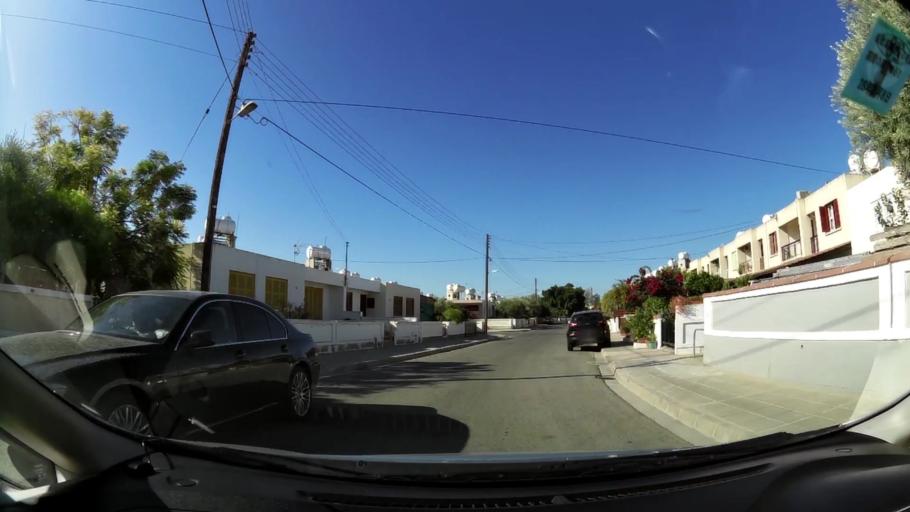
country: CY
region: Larnaka
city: Larnaca
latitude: 34.9336
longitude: 33.6133
